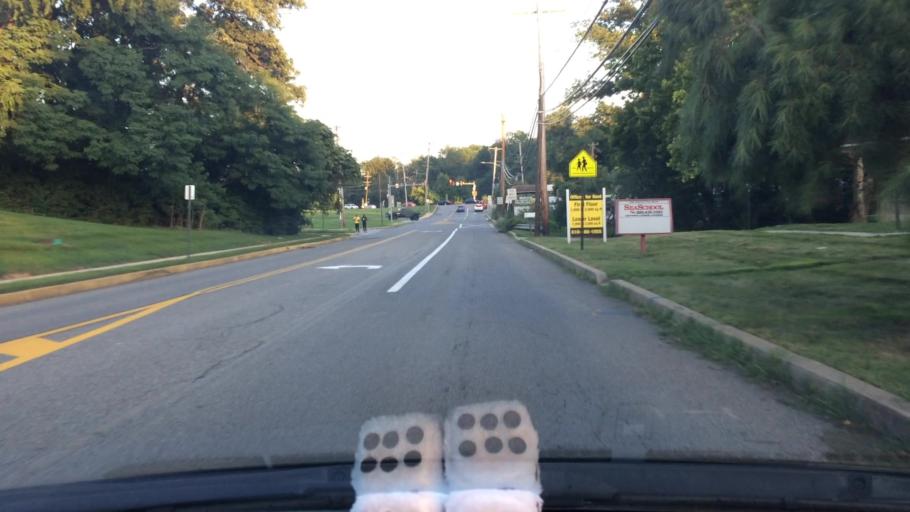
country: US
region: Pennsylvania
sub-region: Delaware County
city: Village Green-Green Ridge
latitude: 39.8507
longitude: -75.4400
